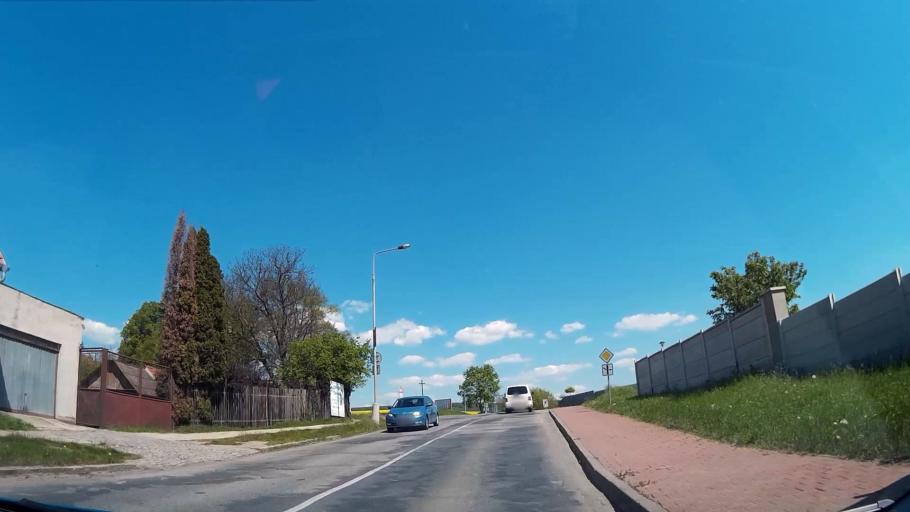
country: CZ
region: South Moravian
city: Ivancice
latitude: 49.1070
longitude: 16.3724
